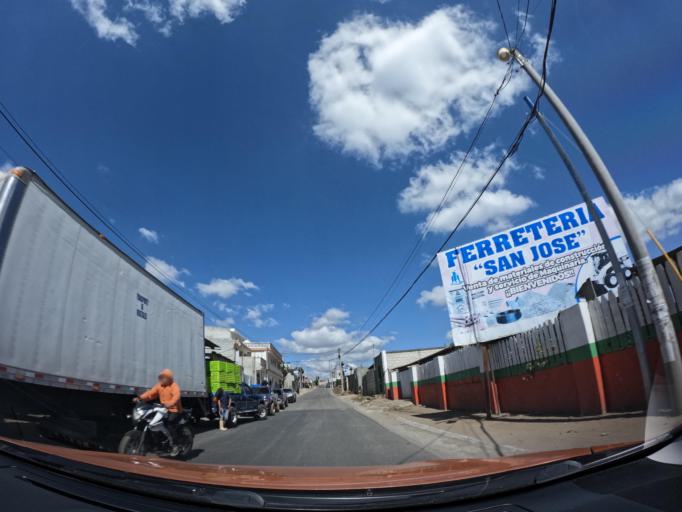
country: GT
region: Chimaltenango
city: Patzun
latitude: 14.6693
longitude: -91.0111
